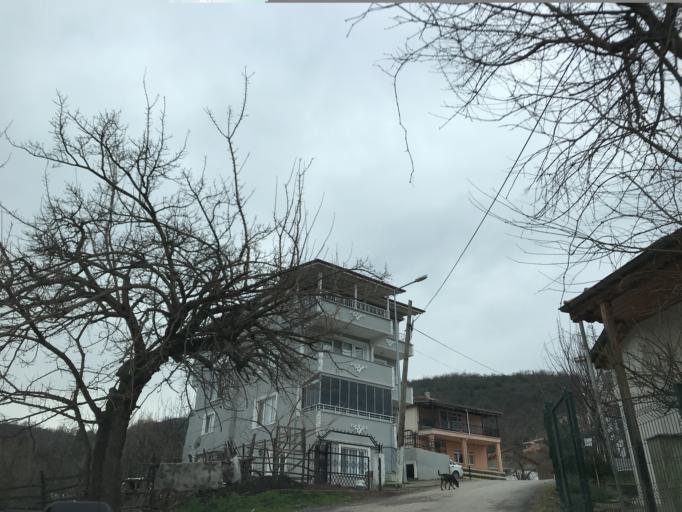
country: TR
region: Yalova
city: Termal
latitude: 40.5964
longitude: 29.1725
